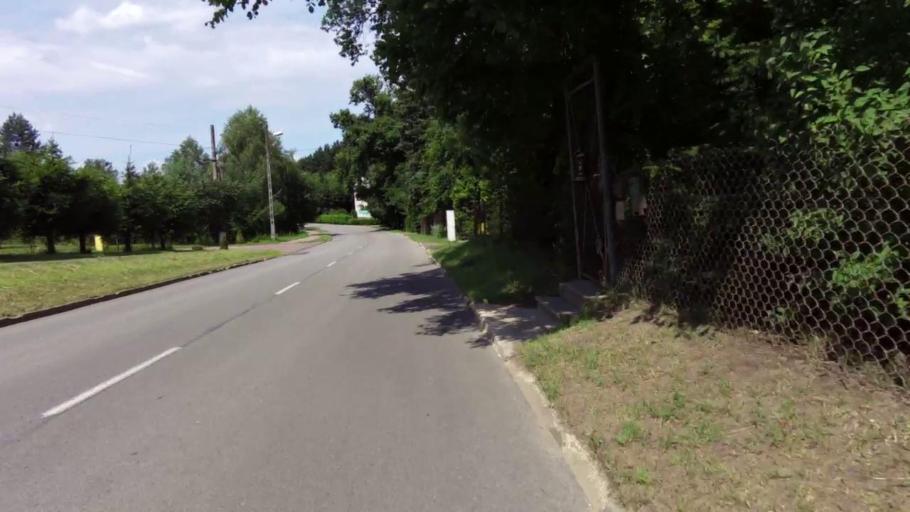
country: PL
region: West Pomeranian Voivodeship
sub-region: Powiat gryfinski
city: Stare Czarnowo
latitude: 53.3436
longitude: 14.7728
